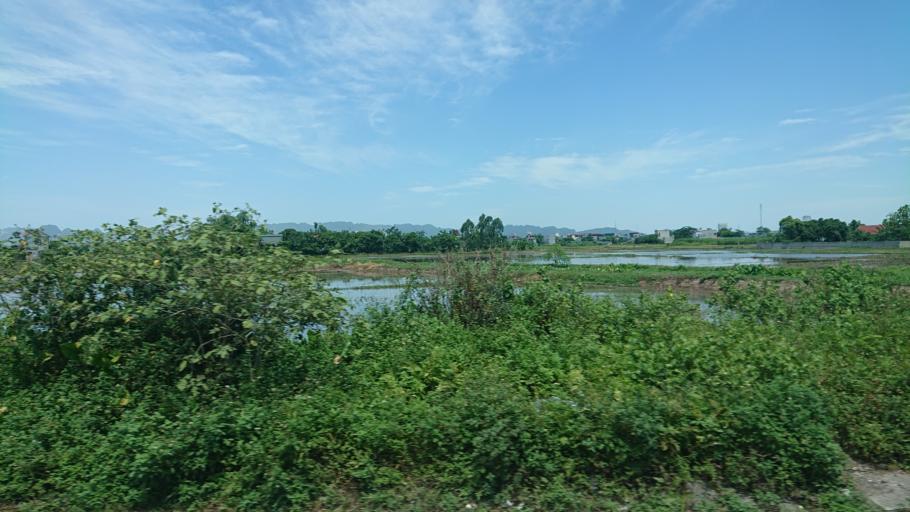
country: VN
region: Ha Nam
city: Thanh Pho Phu Ly
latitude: 20.5267
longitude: 105.9460
